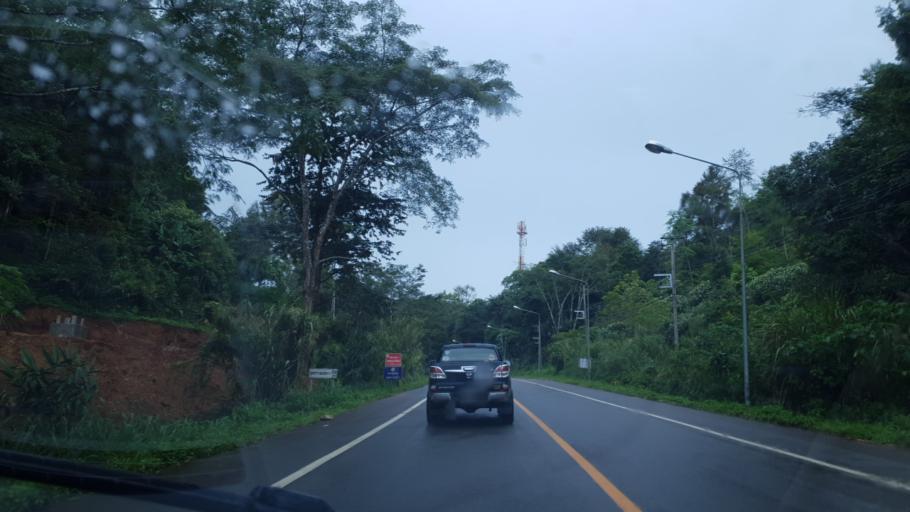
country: TH
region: Mae Hong Son
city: Ban Huai I Huak
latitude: 18.1571
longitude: 98.0669
